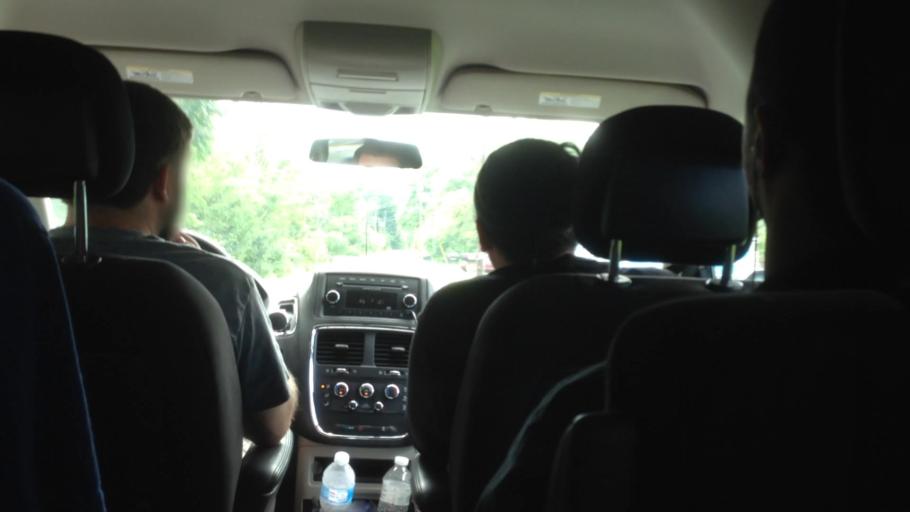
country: US
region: New York
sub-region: Dutchess County
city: Tivoli
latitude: 42.0465
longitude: -73.9044
